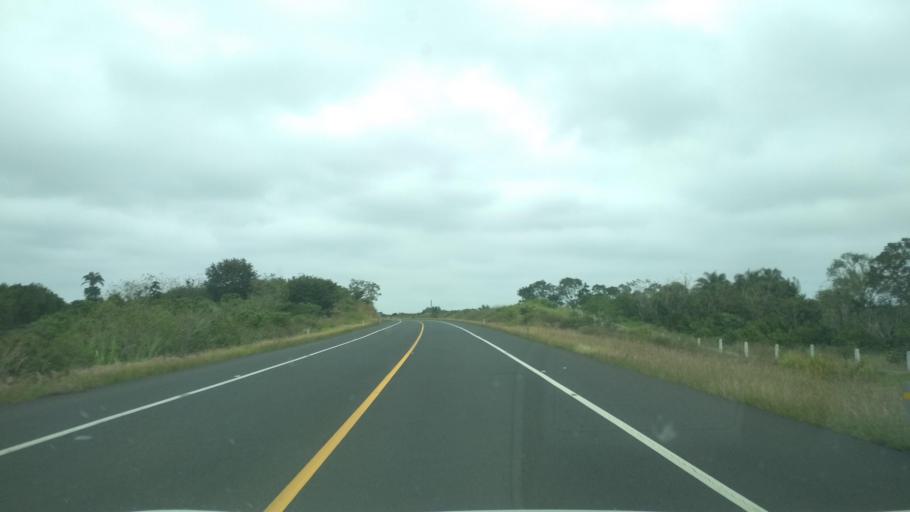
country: MX
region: Veracruz
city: Vega de San Marcos
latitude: 20.1842
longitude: -96.9666
